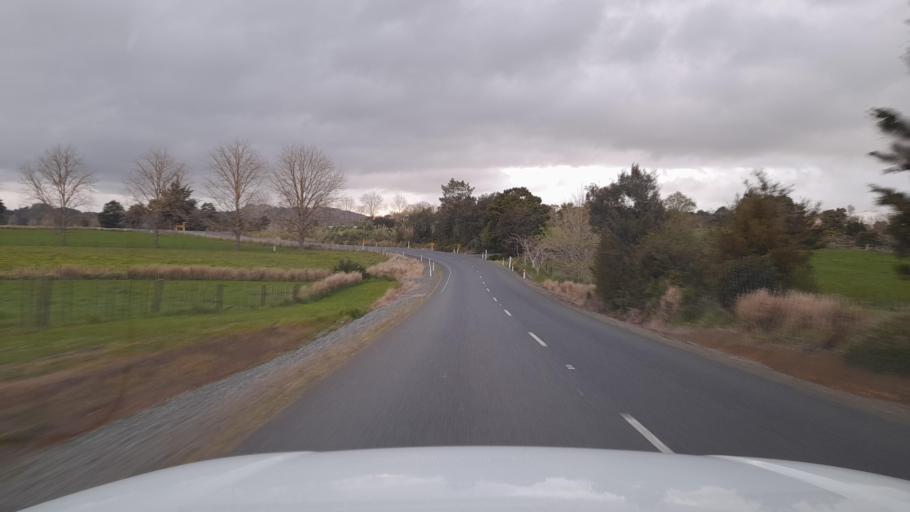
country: NZ
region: Northland
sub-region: Whangarei
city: Maungatapere
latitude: -35.7096
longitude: 174.1809
